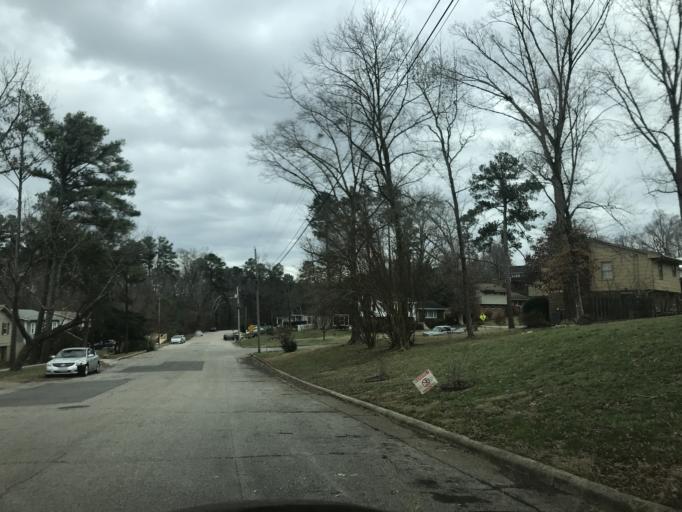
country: US
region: North Carolina
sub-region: Wake County
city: Raleigh
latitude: 35.8002
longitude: -78.6014
